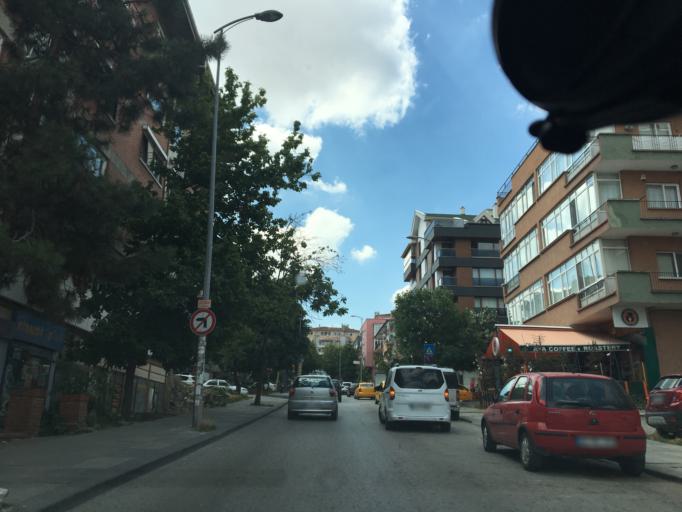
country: TR
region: Ankara
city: Ankara
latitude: 39.8982
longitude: 32.8535
